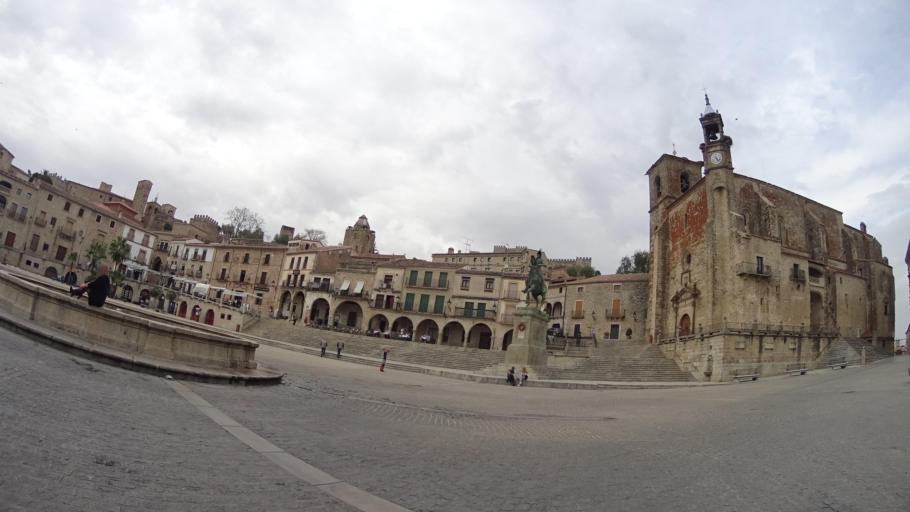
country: ES
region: Extremadura
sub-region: Provincia de Caceres
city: Trujillo
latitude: 39.4605
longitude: -5.8812
